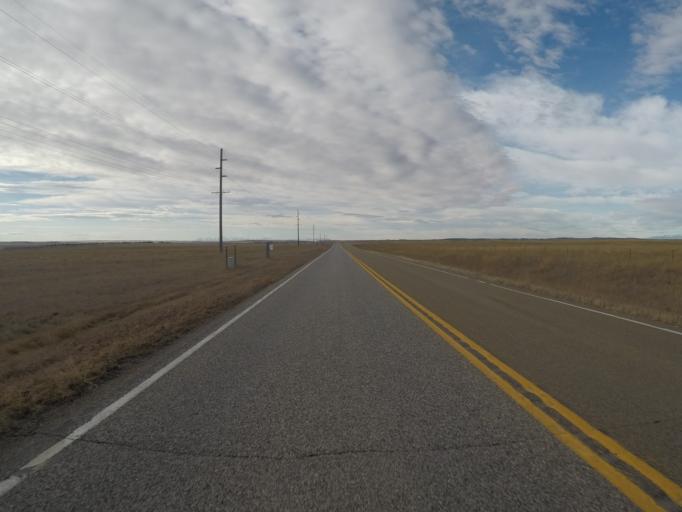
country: US
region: Montana
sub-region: Musselshell County
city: Roundup
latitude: 46.3059
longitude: -108.8485
